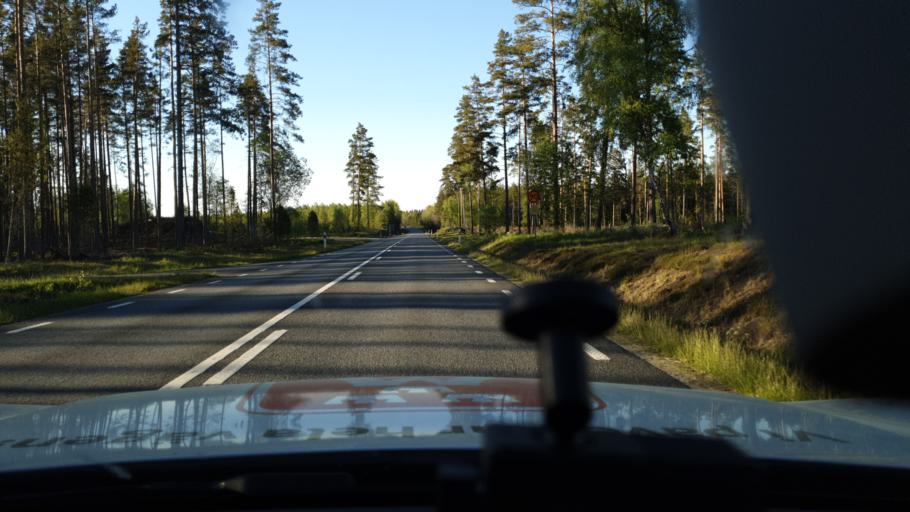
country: SE
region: Joenkoeping
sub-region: Eksjo Kommun
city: Eksjoe
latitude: 57.5895
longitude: 14.9685
